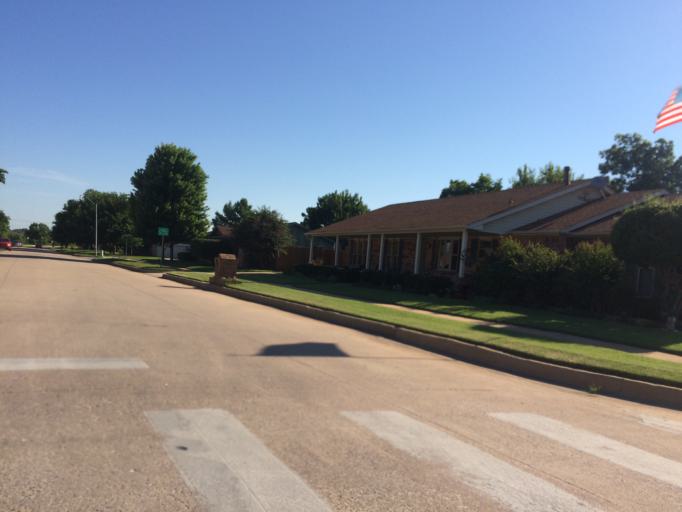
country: US
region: Oklahoma
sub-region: Cleveland County
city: Hall Park
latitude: 35.2381
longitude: -97.4175
